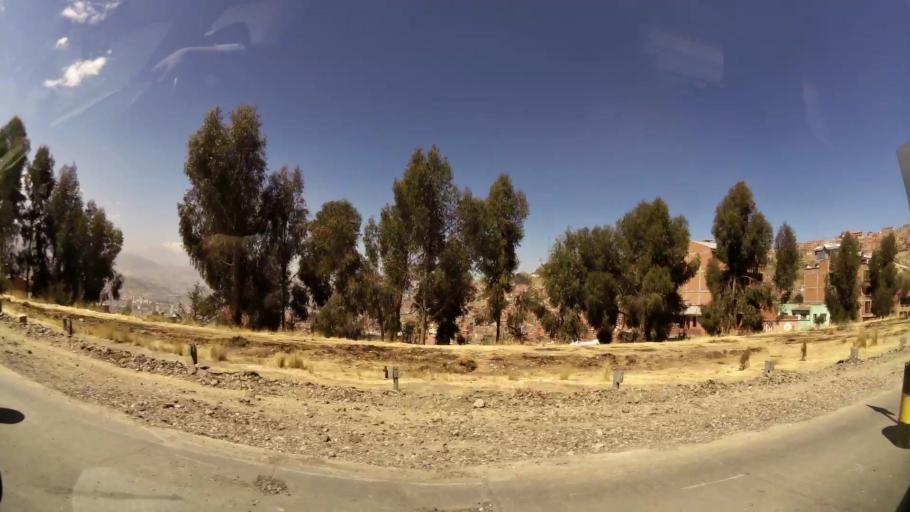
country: BO
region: La Paz
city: La Paz
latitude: -16.4869
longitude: -68.1676
